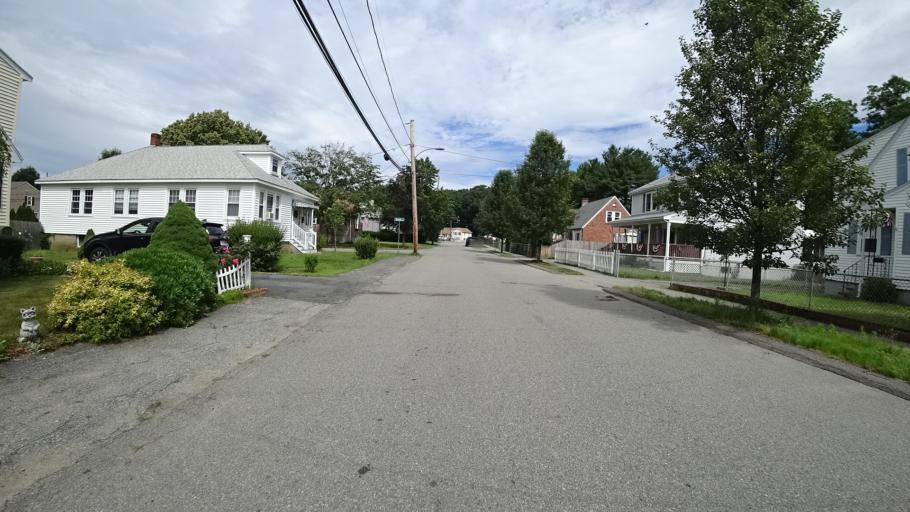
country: US
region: Massachusetts
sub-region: Norfolk County
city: Dedham
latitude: 42.2293
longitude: -71.1418
